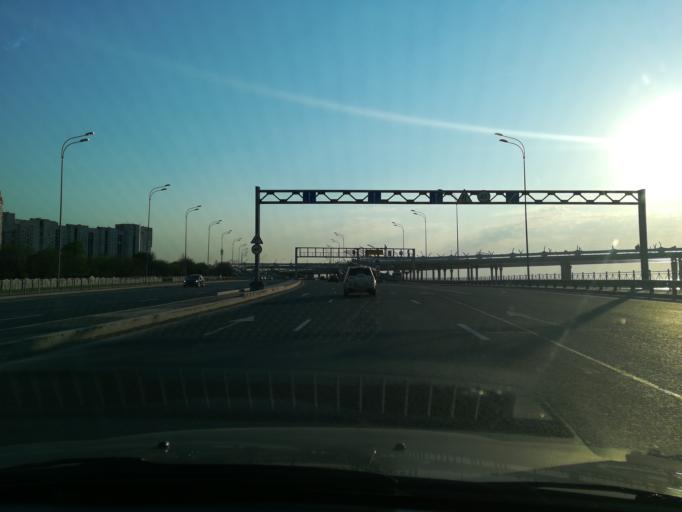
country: RU
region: St.-Petersburg
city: Staraya Derevnya
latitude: 59.9620
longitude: 30.2250
